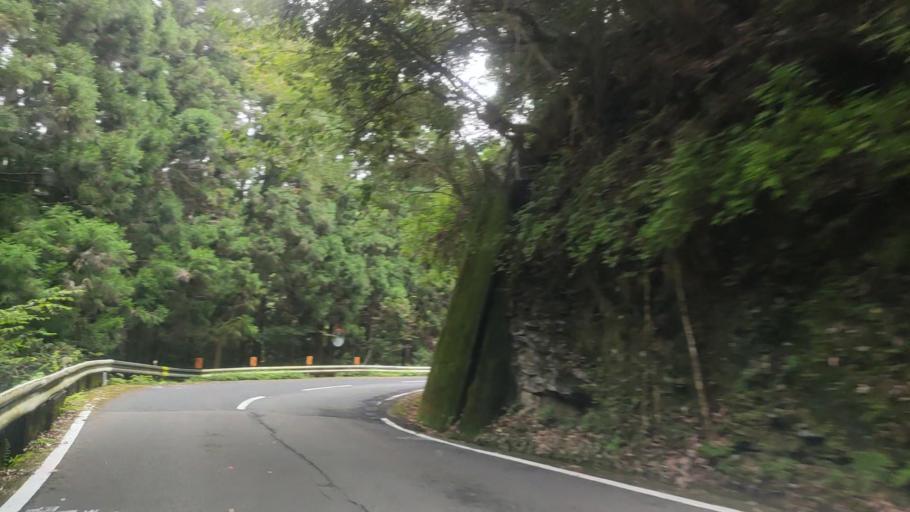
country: JP
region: Wakayama
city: Koya
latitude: 34.2517
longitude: 135.5442
